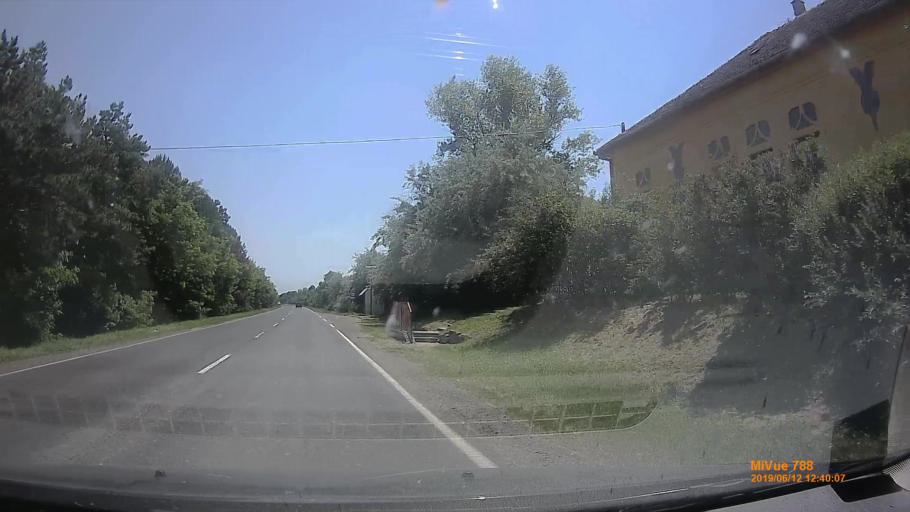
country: HU
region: Bacs-Kiskun
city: Kiskunfelegyhaza
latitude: 46.7585
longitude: 19.8182
